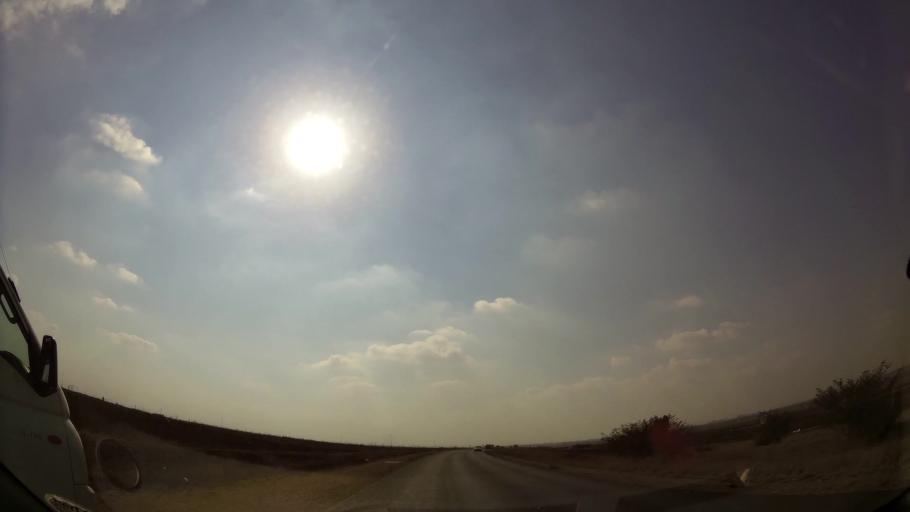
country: ZA
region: Gauteng
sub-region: Ekurhuleni Metropolitan Municipality
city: Springs
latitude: -26.1429
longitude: 28.4470
